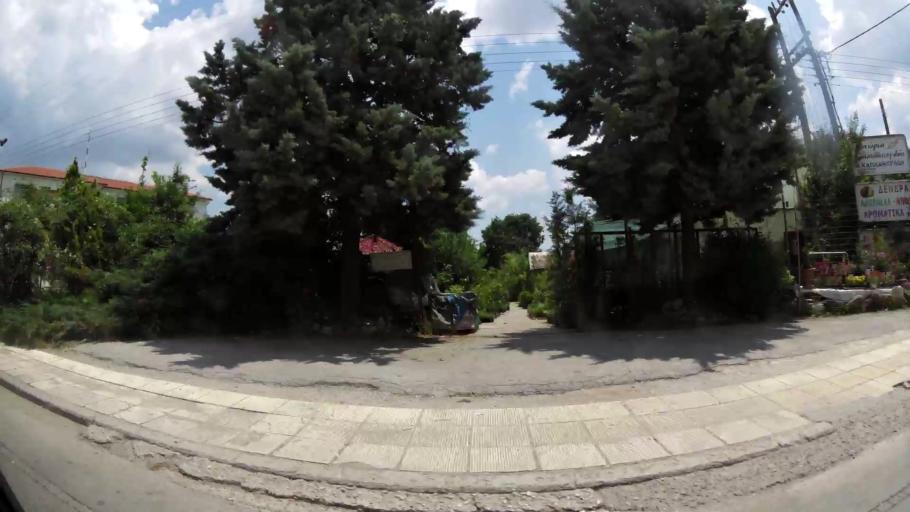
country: GR
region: West Macedonia
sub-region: Nomos Kozanis
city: Kozani
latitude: 40.2876
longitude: 21.7792
